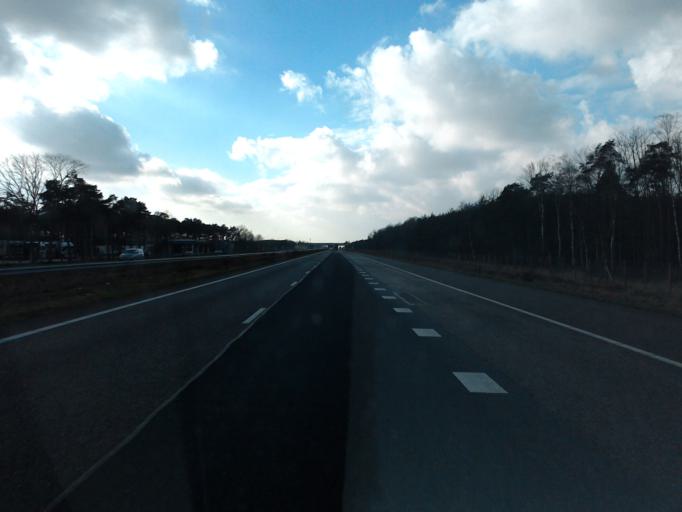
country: NL
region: North Brabant
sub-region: Gemeente Bladel en Netersel
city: Bladel
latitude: 51.3228
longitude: 5.2203
